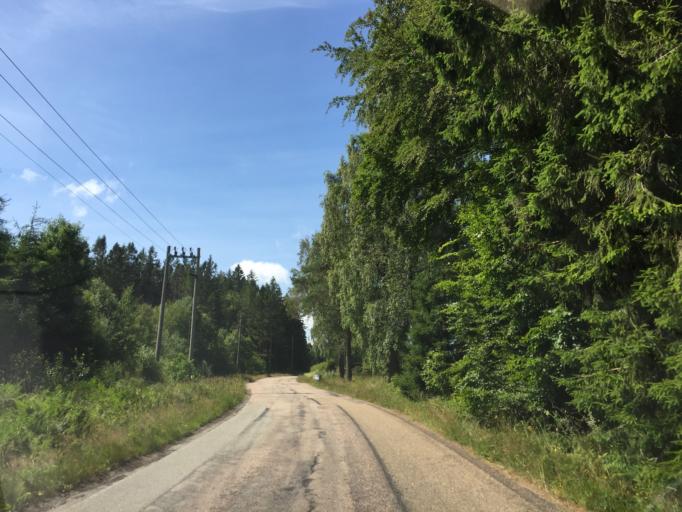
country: SE
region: Vaestra Goetaland
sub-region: Orust
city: Henan
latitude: 58.2966
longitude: 11.6590
